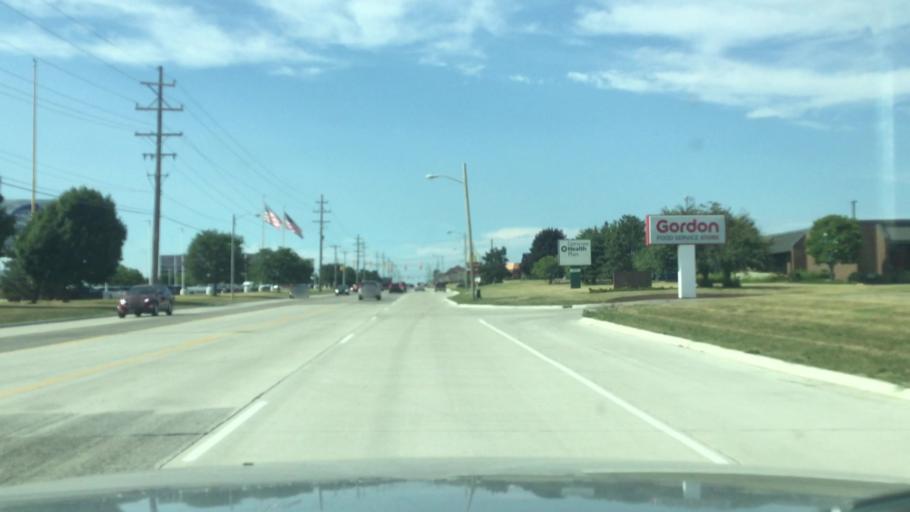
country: US
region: Michigan
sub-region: Genesee County
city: Swartz Creek
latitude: 42.9964
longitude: -83.7725
